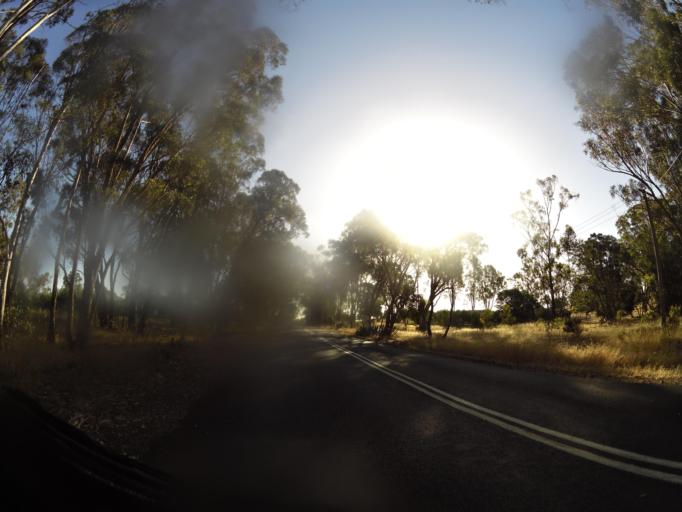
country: AU
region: Victoria
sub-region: Murrindindi
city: Kinglake West
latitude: -37.0207
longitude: 145.1064
